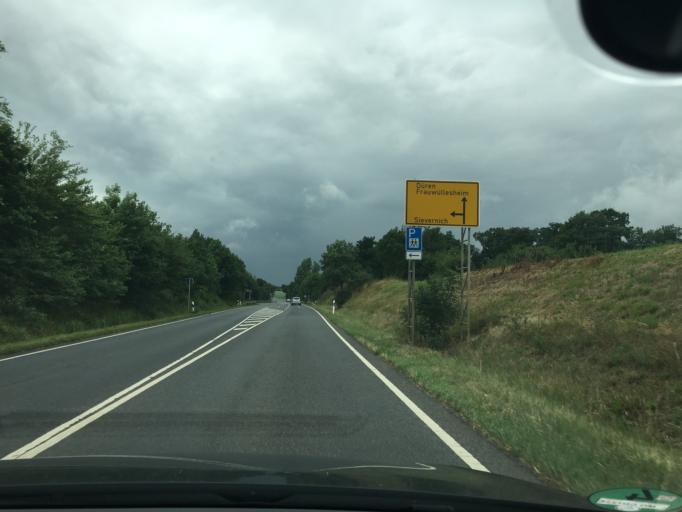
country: DE
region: North Rhine-Westphalia
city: Zulpich
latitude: 50.7280
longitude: 6.6745
